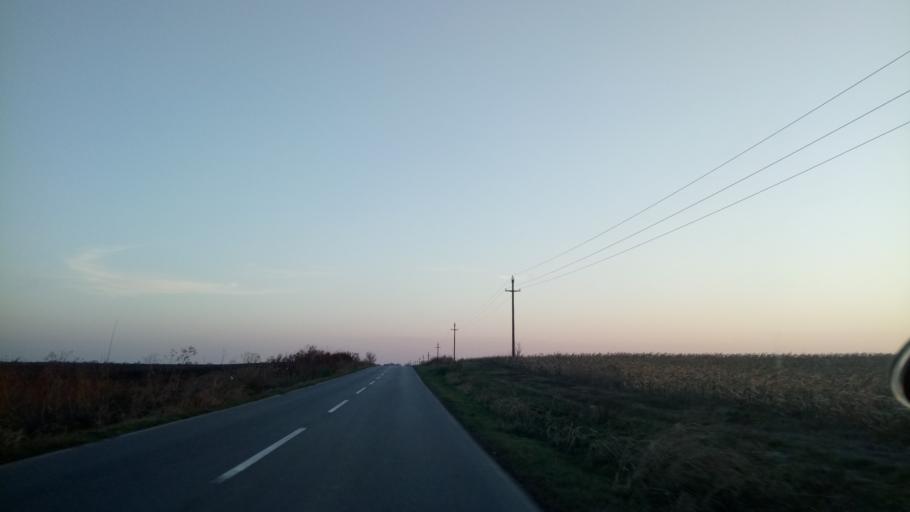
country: RS
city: Belegis
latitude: 45.0405
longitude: 20.3333
